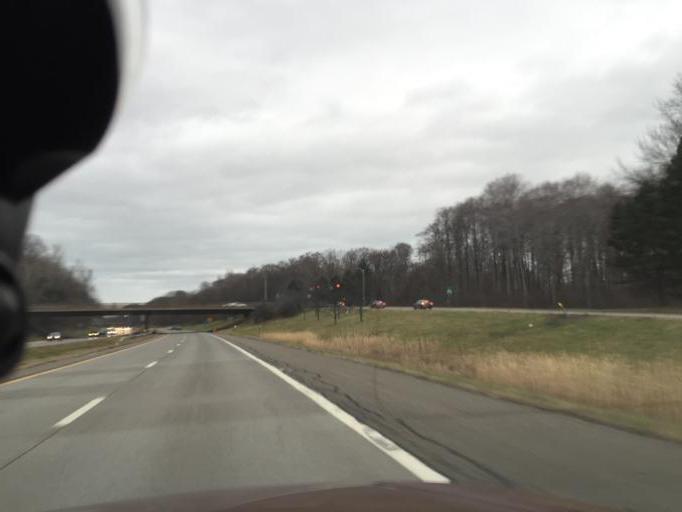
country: US
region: New York
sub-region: Monroe County
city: Greece
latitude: 43.2296
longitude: -77.6725
